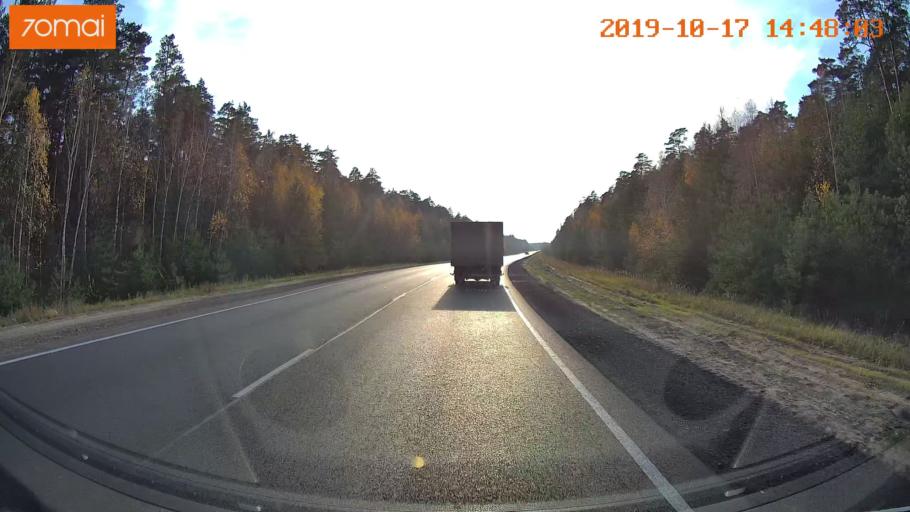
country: RU
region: Rjazan
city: Solotcha
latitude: 54.7633
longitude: 39.8543
